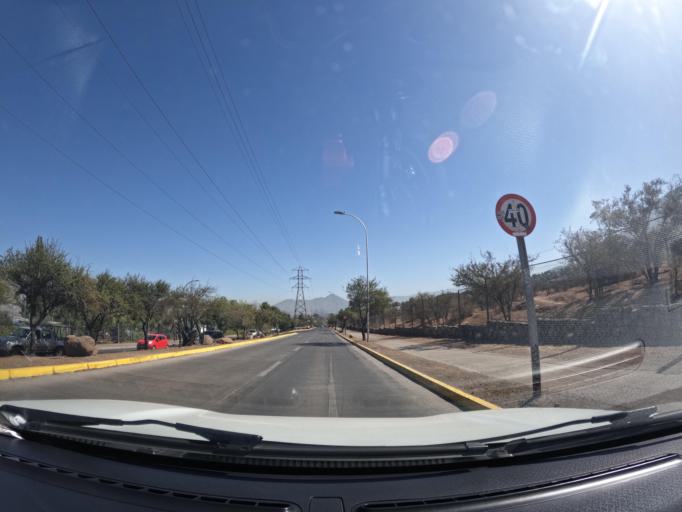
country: CL
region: Santiago Metropolitan
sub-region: Provincia de Santiago
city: Villa Presidente Frei, Nunoa, Santiago, Chile
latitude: -33.4855
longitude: -70.5214
